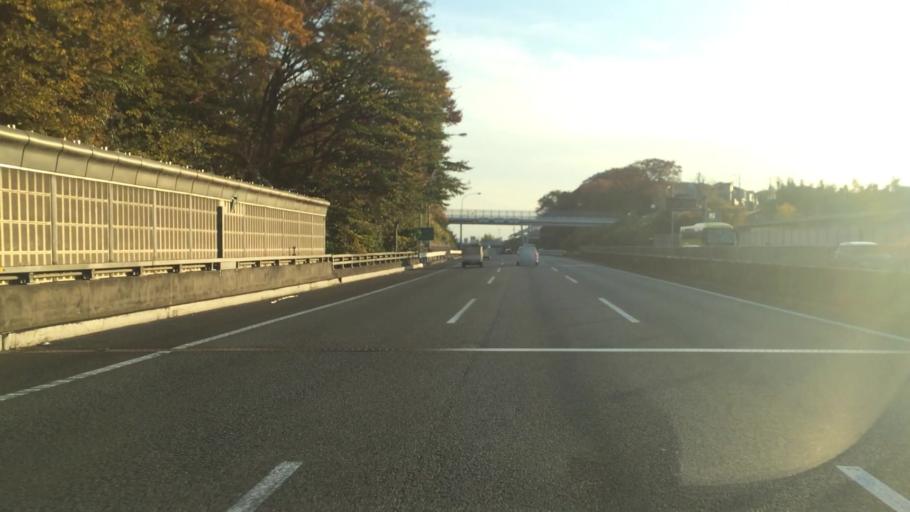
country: JP
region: Tokyo
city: Chofugaoka
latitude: 35.5830
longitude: 139.6187
